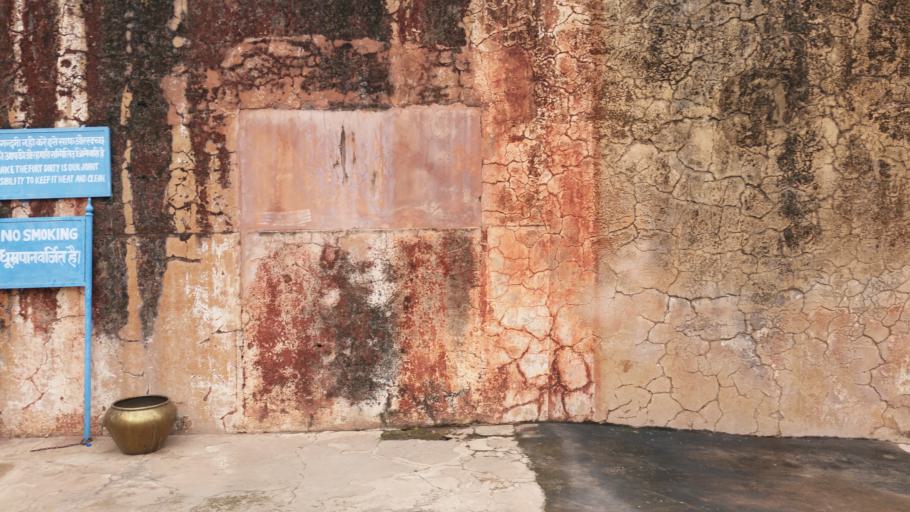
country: IN
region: Rajasthan
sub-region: Jaipur
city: Jaipur
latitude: 26.9849
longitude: 75.8454
